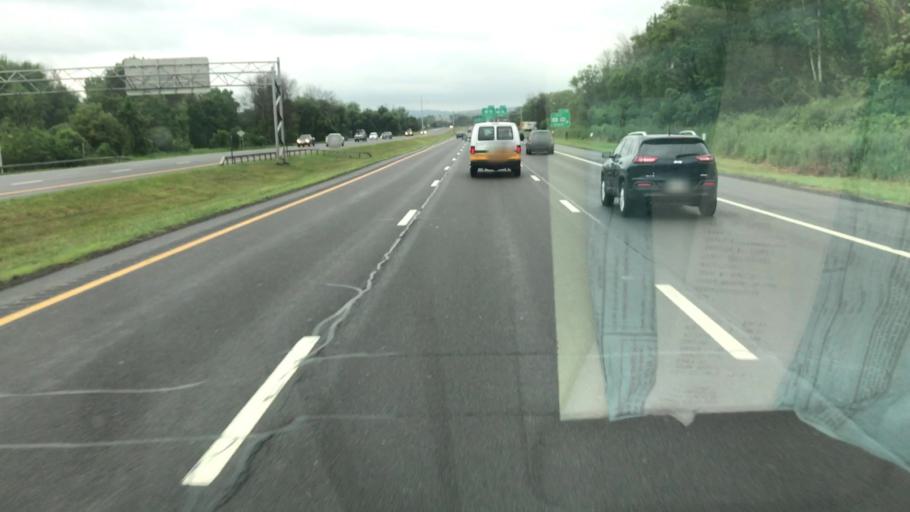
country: US
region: New York
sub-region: Onondaga County
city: East Syracuse
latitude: 43.0395
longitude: -76.0547
